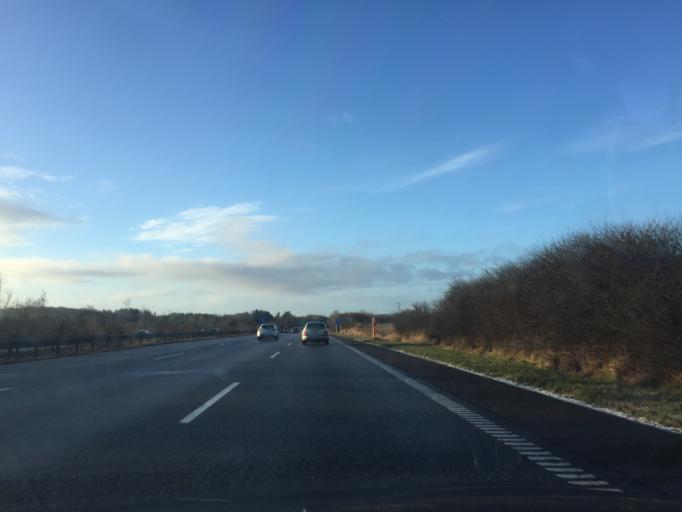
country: DK
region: South Denmark
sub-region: Kolding Kommune
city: Kolding
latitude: 55.5399
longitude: 9.5108
